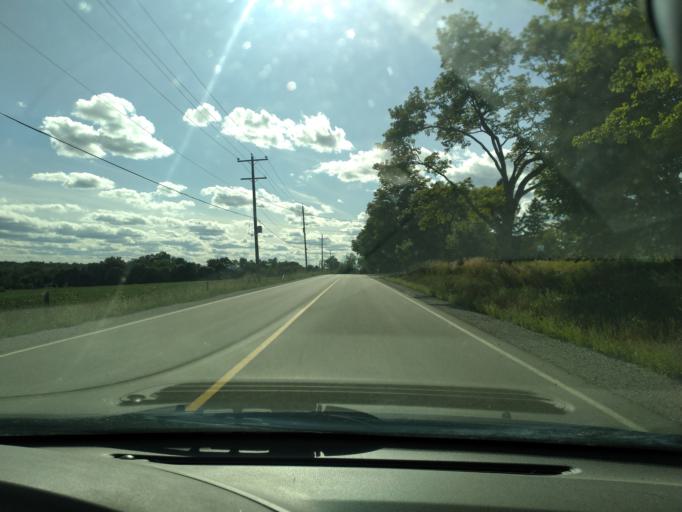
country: CA
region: Ontario
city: Bradford West Gwillimbury
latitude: 44.0781
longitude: -79.6695
